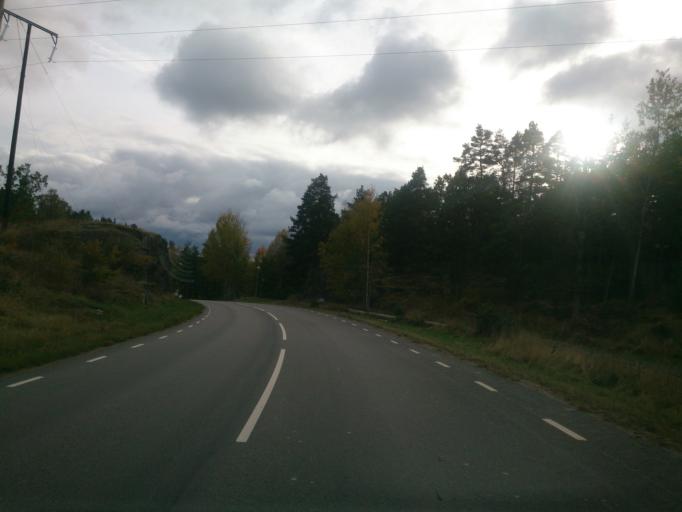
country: SE
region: OEstergoetland
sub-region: Atvidabergs Kommun
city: Atvidaberg
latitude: 58.2134
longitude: 16.0128
